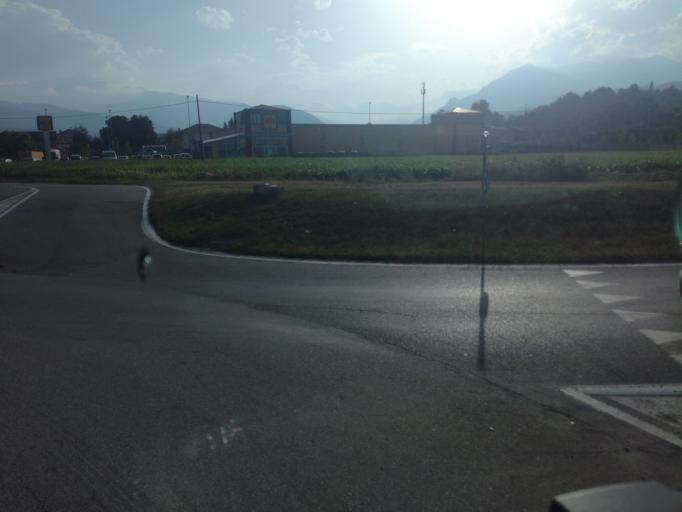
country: IT
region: Piedmont
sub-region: Provincia di Torino
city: Bricherasio
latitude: 44.8257
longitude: 7.3124
